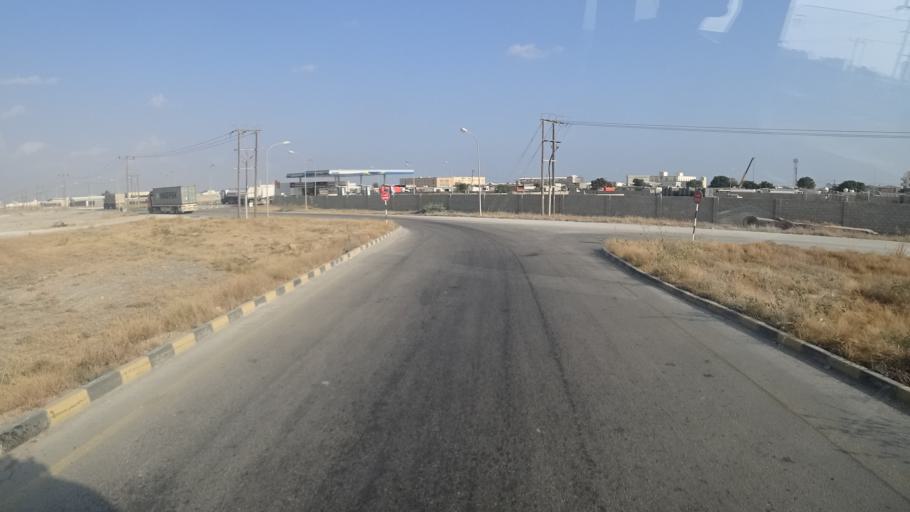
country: OM
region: Zufar
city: Salalah
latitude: 17.0343
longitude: 54.0358
